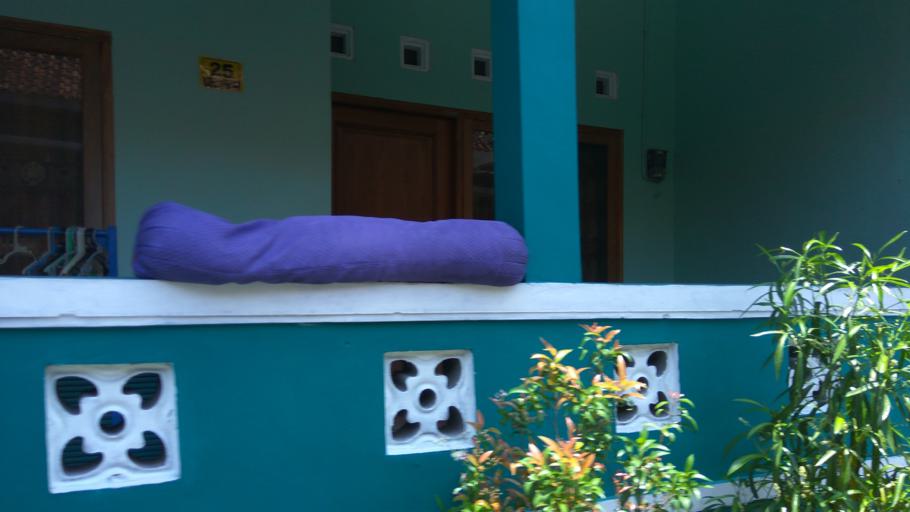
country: ID
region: Central Java
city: Grogol
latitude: -7.5907
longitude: 110.7985
